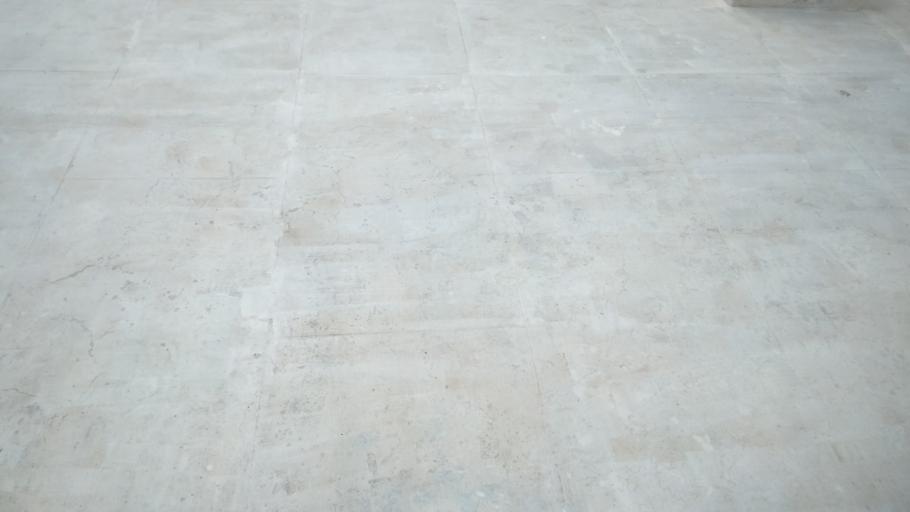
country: IN
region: Tamil Nadu
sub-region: Coimbatore
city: Periyanayakkanpalaiyam
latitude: 11.0887
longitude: 76.9173
